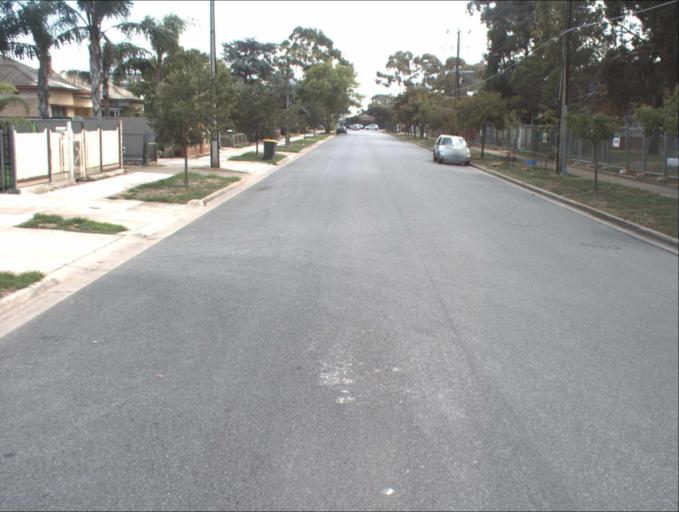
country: AU
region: South Australia
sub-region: Charles Sturt
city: Woodville
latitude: -34.8779
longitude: 138.5574
